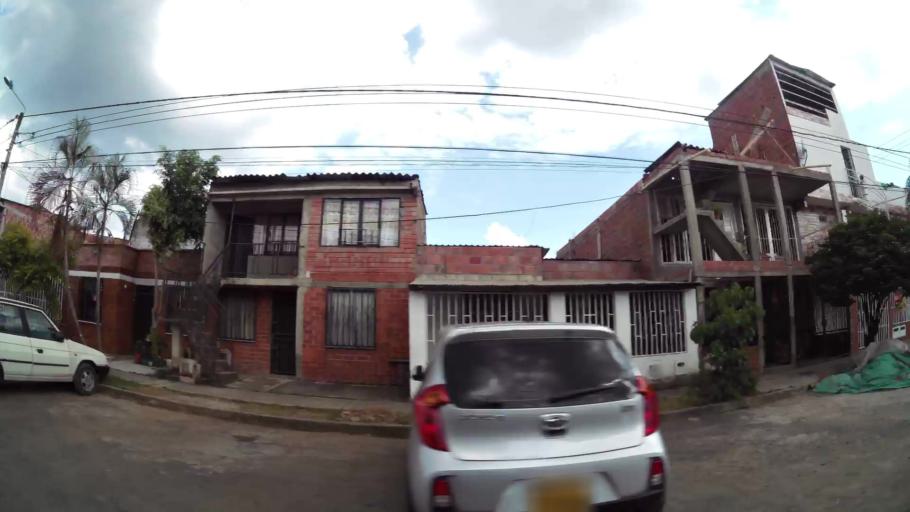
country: CO
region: Valle del Cauca
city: Cali
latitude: 3.4020
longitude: -76.5016
